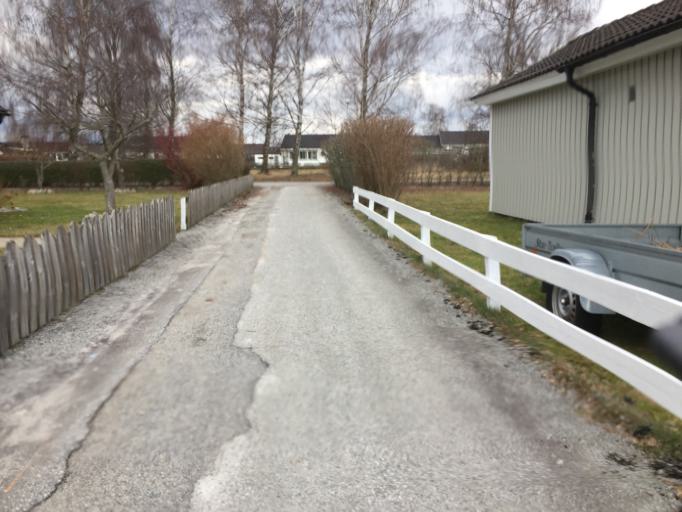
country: SE
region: Blekinge
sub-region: Karlshamns Kommun
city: Morrum
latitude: 56.1872
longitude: 14.7539
